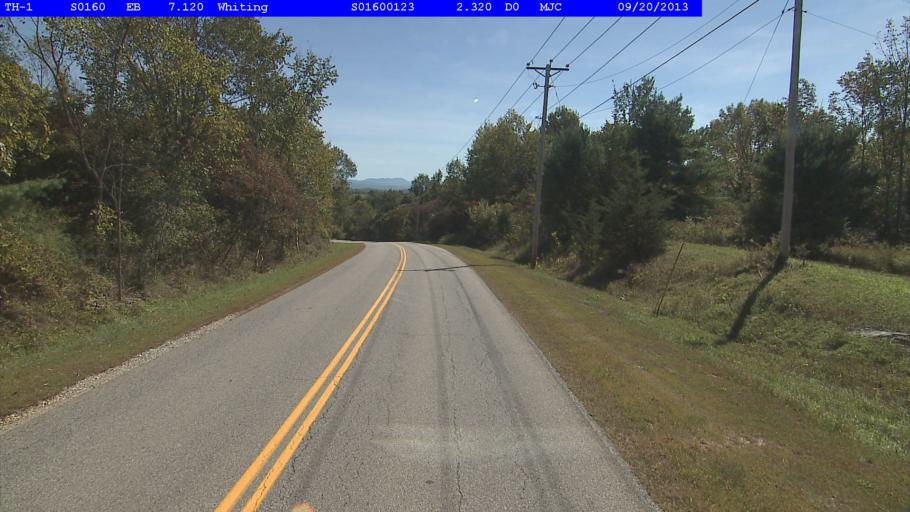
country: US
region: Vermont
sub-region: Rutland County
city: Brandon
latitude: 43.8558
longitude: -73.1835
